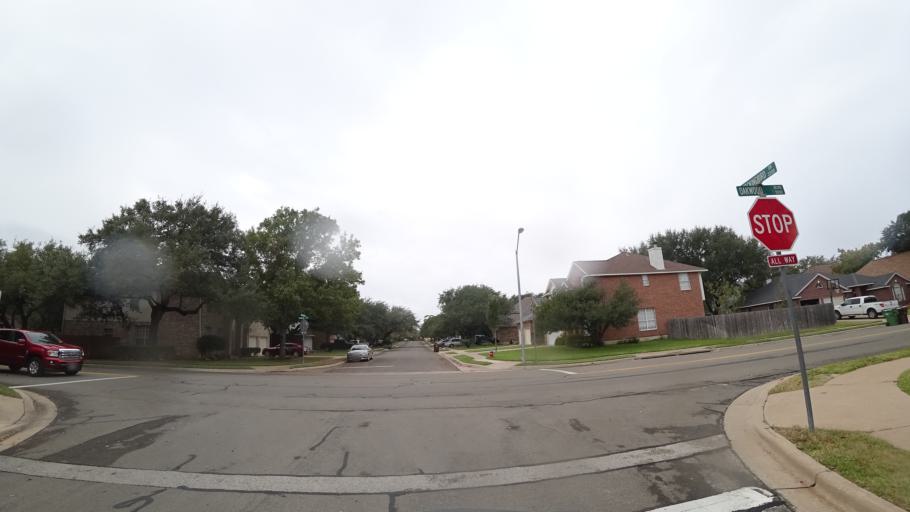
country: US
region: Texas
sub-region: Williamson County
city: Brushy Creek
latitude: 30.5161
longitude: -97.7109
